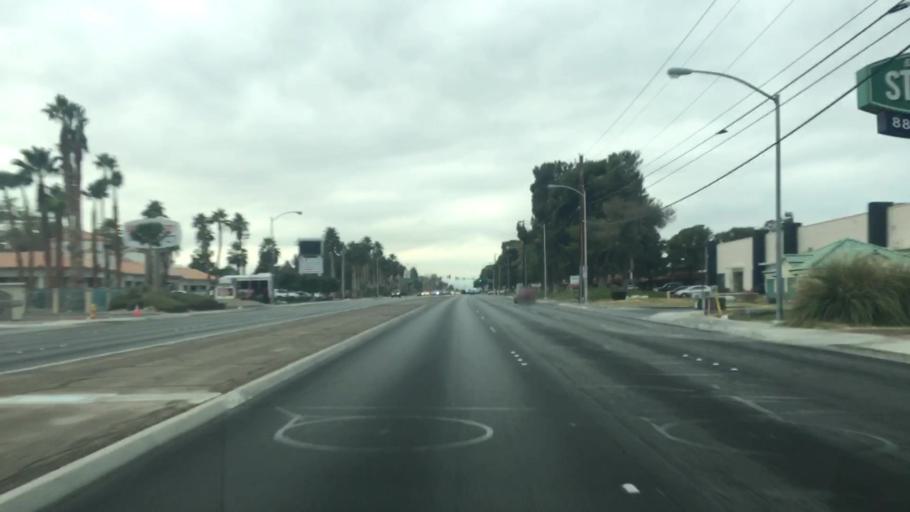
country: US
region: Nevada
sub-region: Clark County
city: Whitney
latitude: 36.0716
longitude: -115.1090
